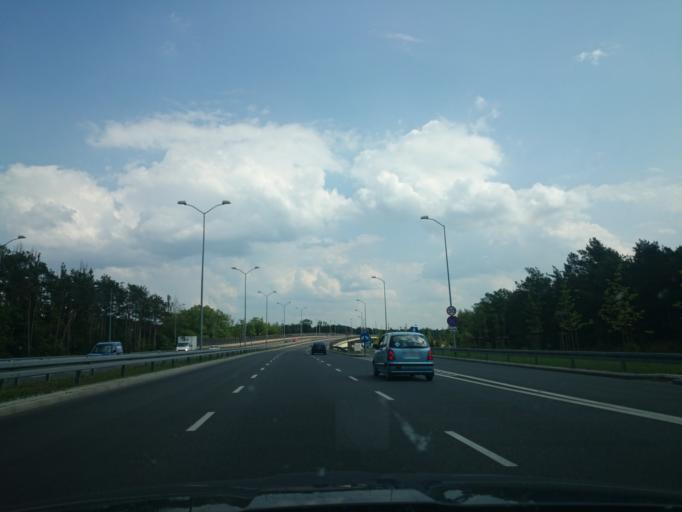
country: PL
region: West Pomeranian Voivodeship
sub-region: Szczecin
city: Szczecin
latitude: 53.3819
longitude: 14.6784
